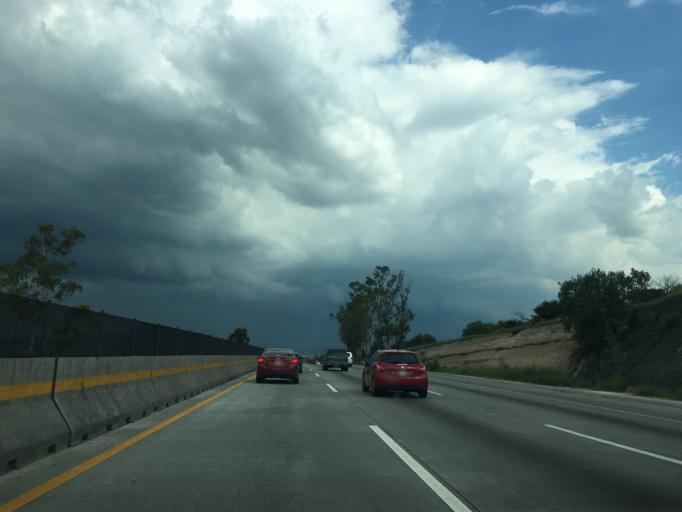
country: MX
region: Hidalgo
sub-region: Tepeji del Rio de Ocampo
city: Santiago Tlautla
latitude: 19.9273
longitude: -99.3766
